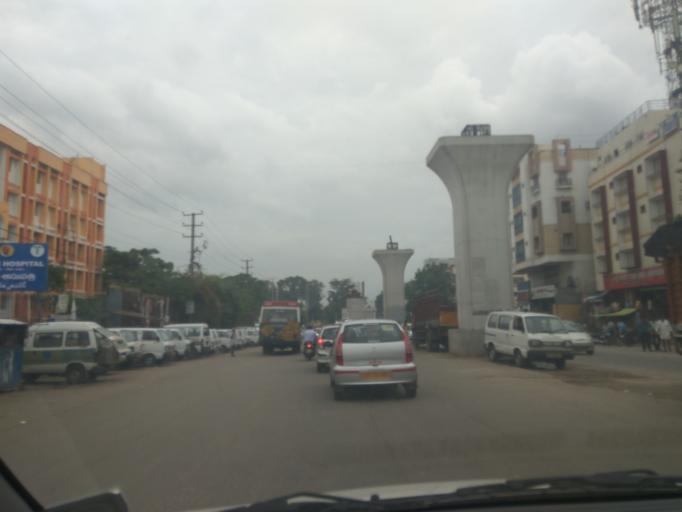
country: IN
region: Telangana
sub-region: Hyderabad
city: Malkajgiri
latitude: 17.4237
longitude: 78.5018
